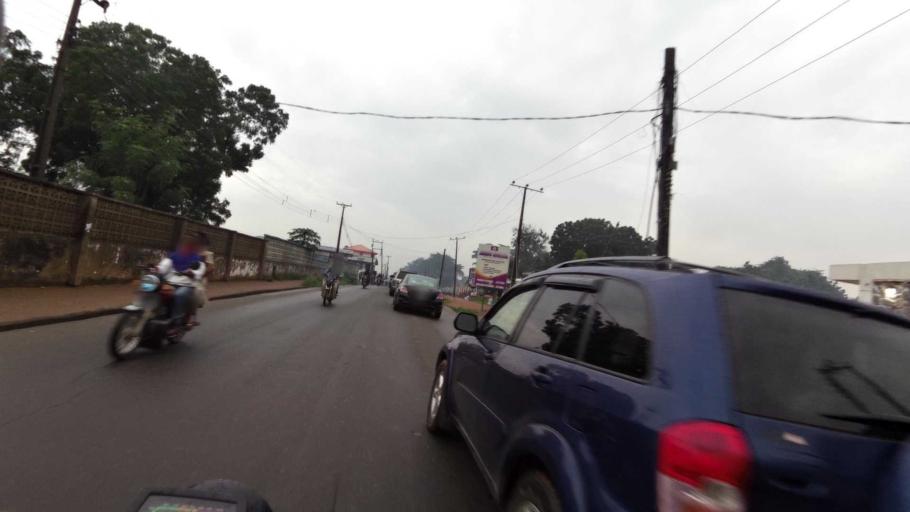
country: NG
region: Oyo
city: Ibadan
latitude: 7.4103
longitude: 3.9298
